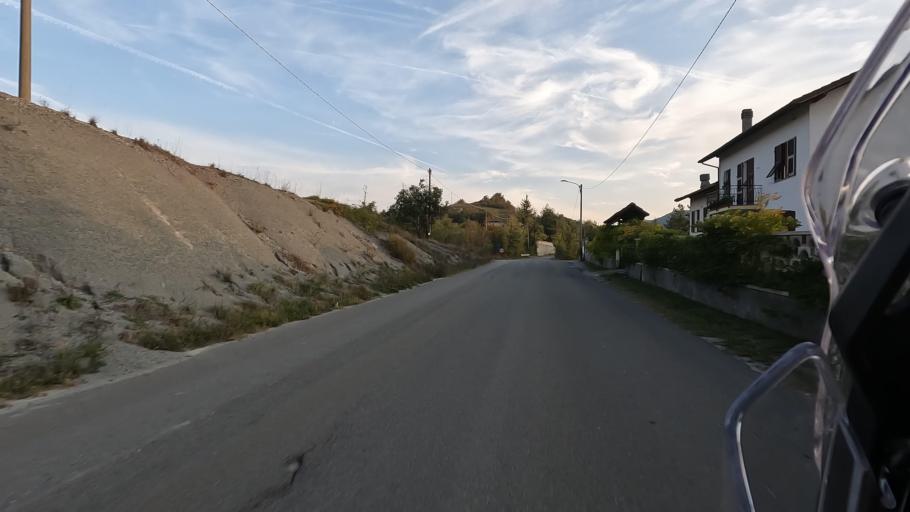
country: IT
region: Liguria
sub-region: Provincia di Savona
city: Mioglia
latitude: 44.4804
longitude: 8.4138
